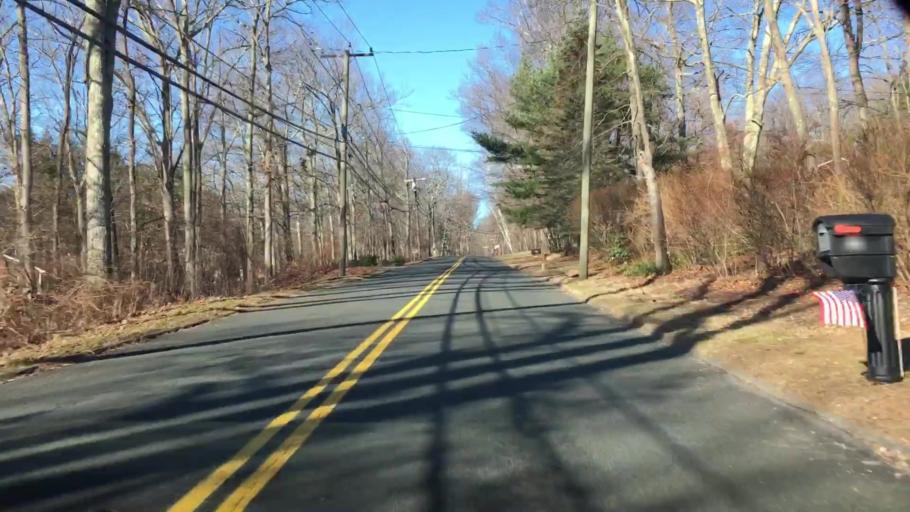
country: US
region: Connecticut
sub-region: Tolland County
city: Crystal Lake
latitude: 41.9356
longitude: -72.3878
